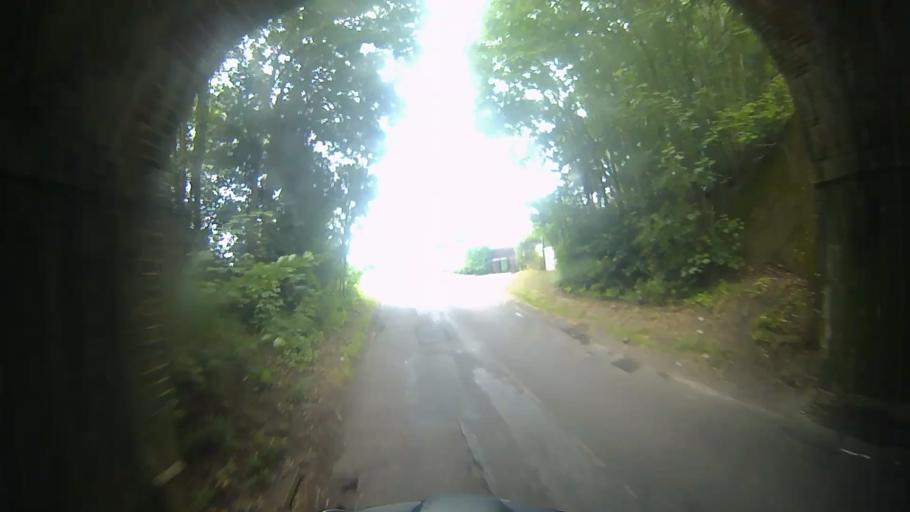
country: GB
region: England
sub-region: Hampshire
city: Kingsley
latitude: 51.1796
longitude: -0.8725
